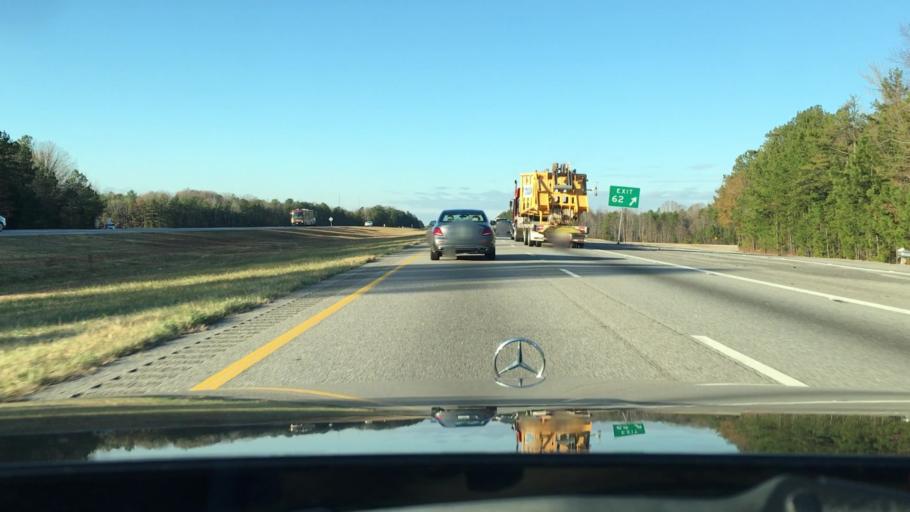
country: US
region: South Carolina
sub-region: Chester County
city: Eureka Mill
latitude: 34.7093
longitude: -81.0306
